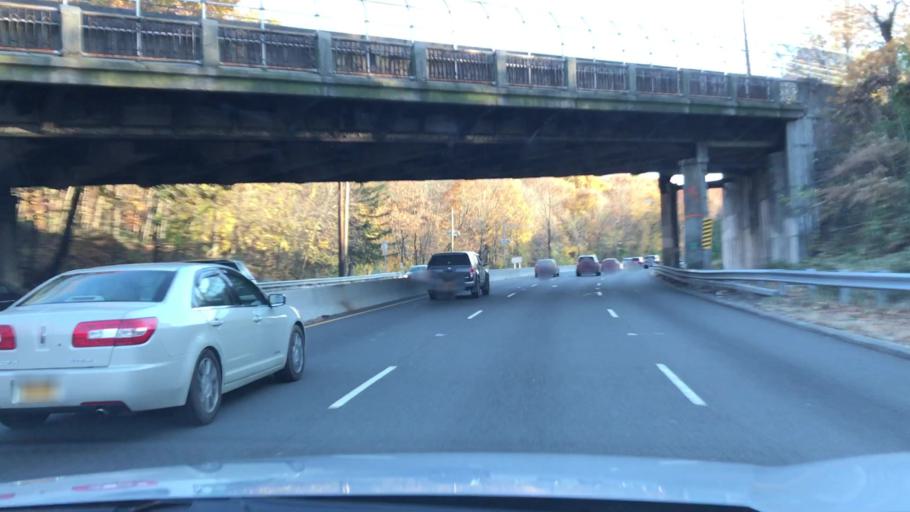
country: US
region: New Jersey
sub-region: Bergen County
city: Englewood
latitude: 40.8737
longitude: -73.9730
